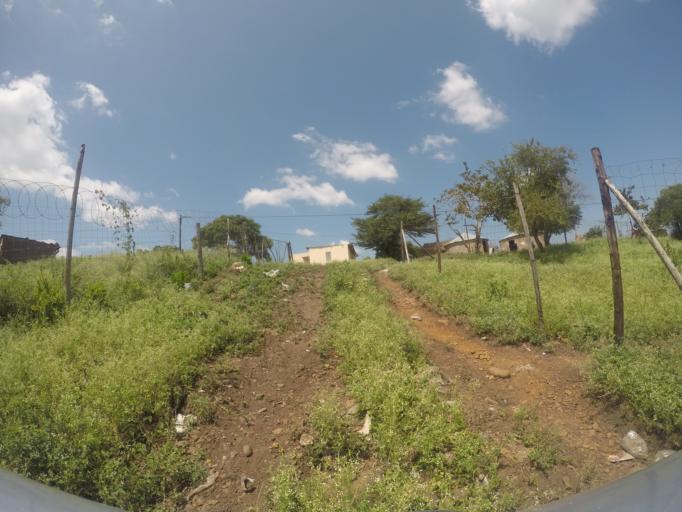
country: ZA
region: KwaZulu-Natal
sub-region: uThungulu District Municipality
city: Empangeni
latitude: -28.6087
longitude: 31.7360
